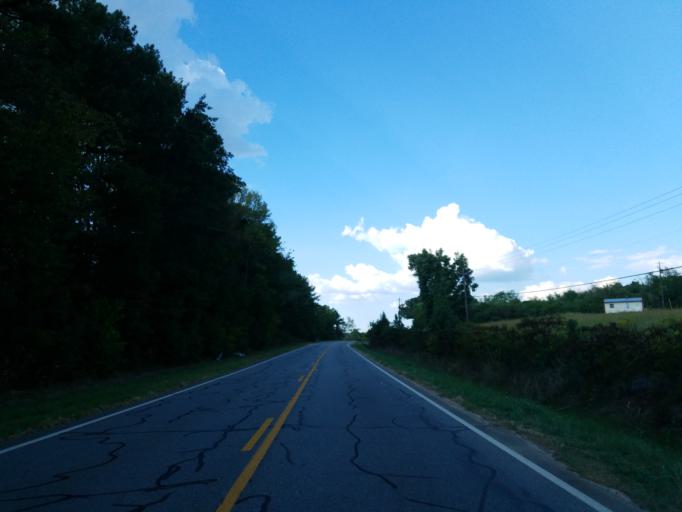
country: US
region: Georgia
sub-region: Bartow County
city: Rydal
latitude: 34.5139
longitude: -84.7100
